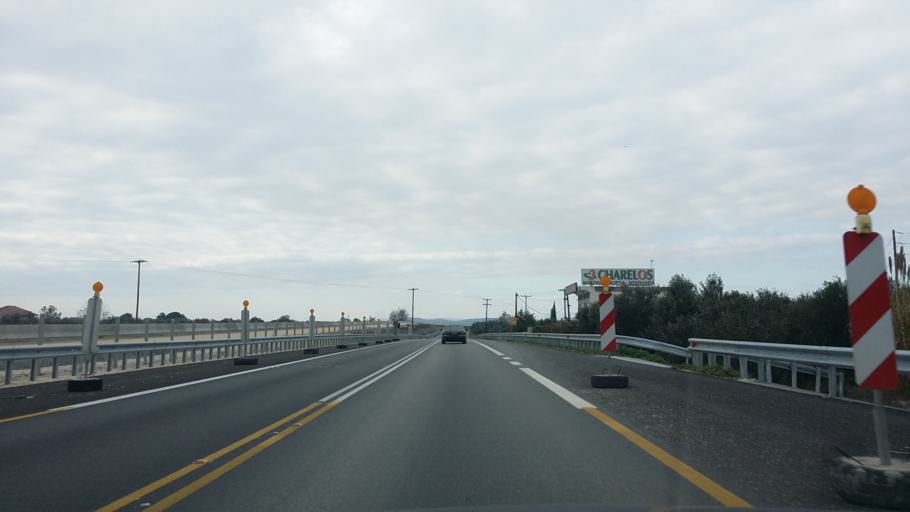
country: GR
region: West Greece
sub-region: Nomos Aitolias kai Akarnanias
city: Mesolongi
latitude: 38.3984
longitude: 21.4137
